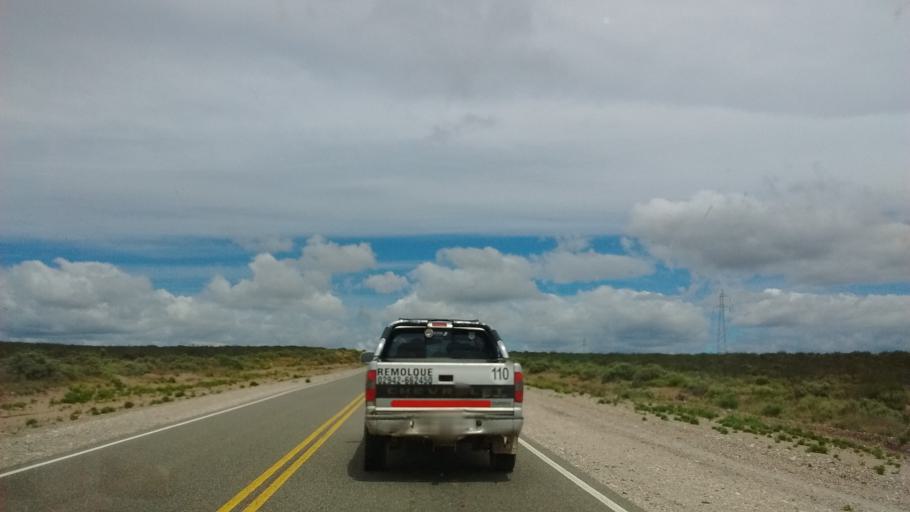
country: AR
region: Neuquen
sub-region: Departamento de Picun Leufu
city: Picun Leufu
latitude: -39.7346
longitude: -69.5877
